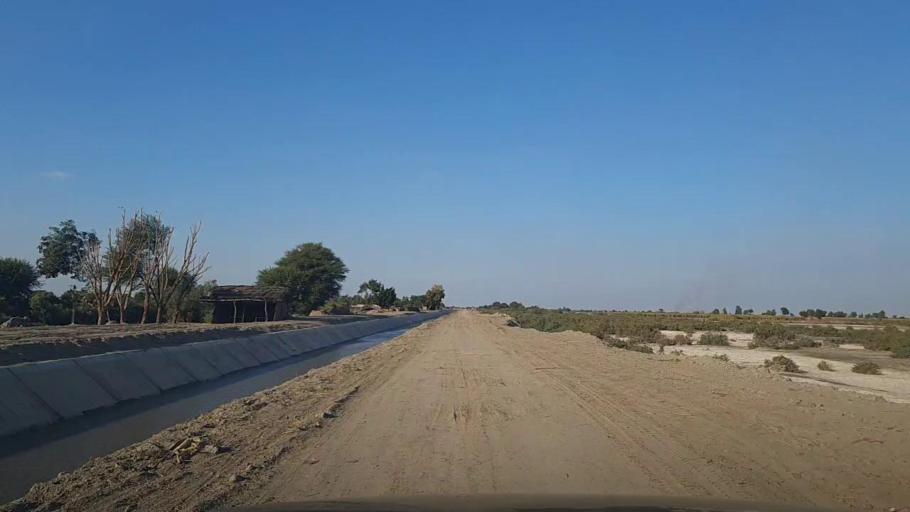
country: PK
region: Sindh
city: Jhol
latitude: 25.9121
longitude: 69.0403
